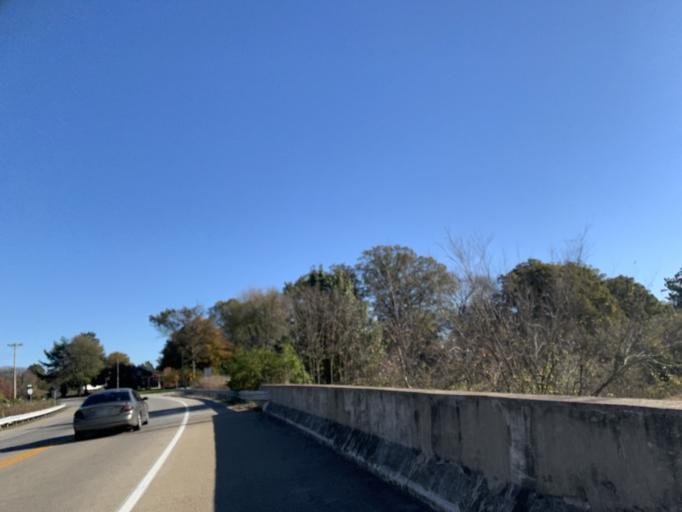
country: US
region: Kentucky
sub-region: Jefferson County
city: Pleasure Ridge Park
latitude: 38.1456
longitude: -85.8839
